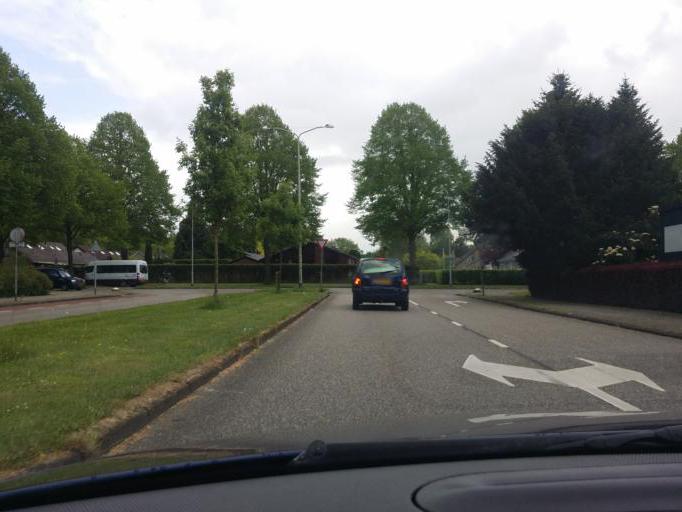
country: NL
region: Groningen
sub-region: Gemeente Hoogezand-Sappemeer
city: Hoogezand
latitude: 53.1558
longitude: 6.7402
